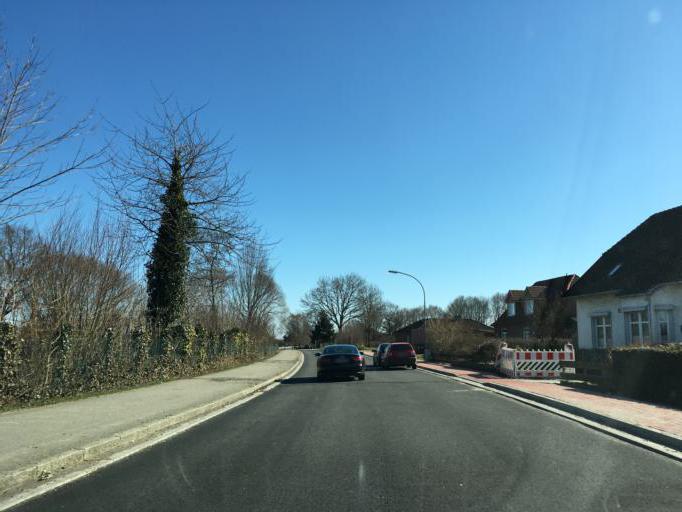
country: DE
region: Schleswig-Holstein
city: Kastorf
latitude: 53.7440
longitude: 10.5811
